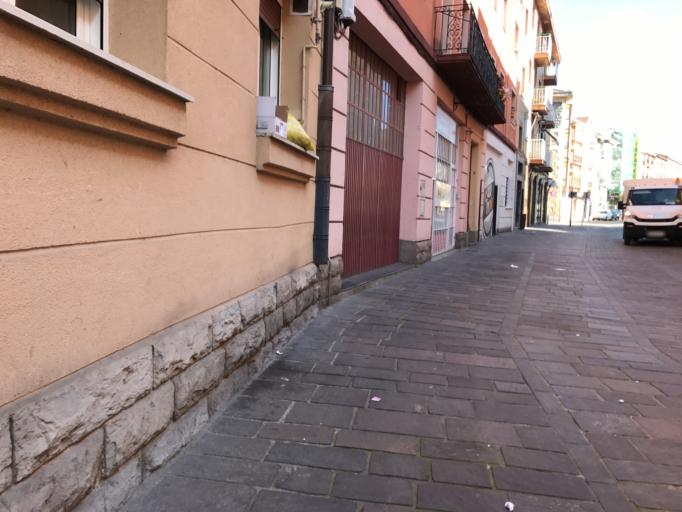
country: ES
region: Basque Country
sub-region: Provincia de Alava
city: Gasteiz / Vitoria
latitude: 42.8521
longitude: -2.6713
